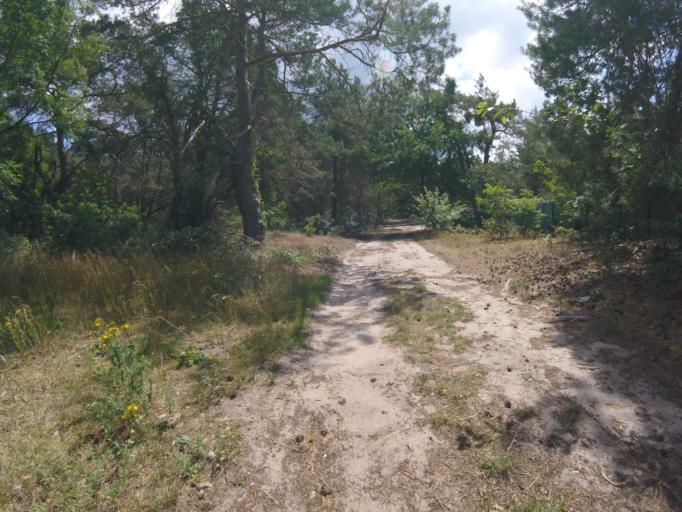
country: DE
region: Brandenburg
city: Bestensee
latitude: 52.2207
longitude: 13.6254
